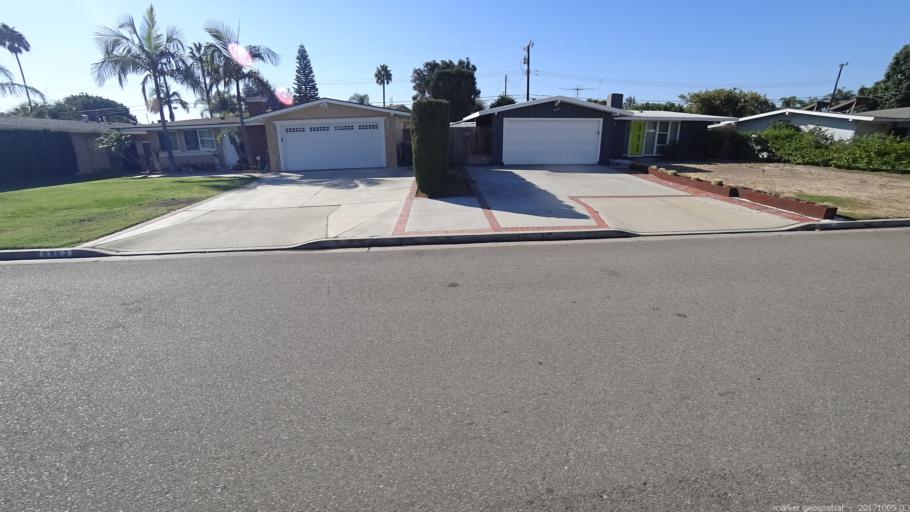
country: US
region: California
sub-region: Orange County
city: Stanton
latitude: 33.7997
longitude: -117.9610
